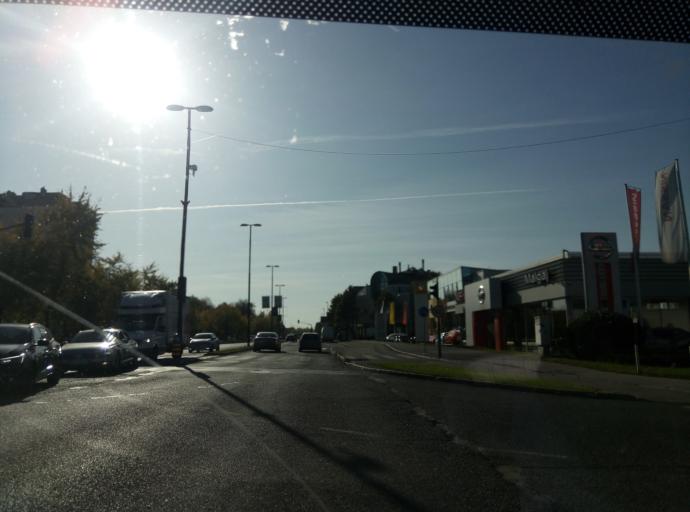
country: SI
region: Ljubljana
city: Ljubljana
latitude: 46.0406
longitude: 14.4740
